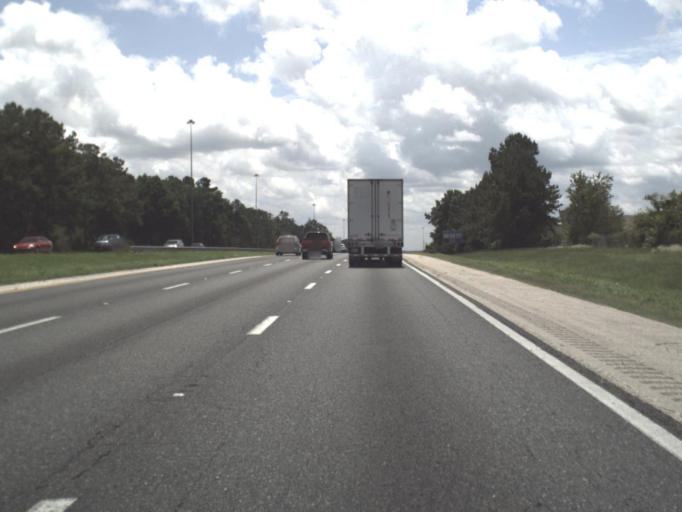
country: US
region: Florida
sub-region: Alachua County
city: Alachua
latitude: 29.6671
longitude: -82.4256
